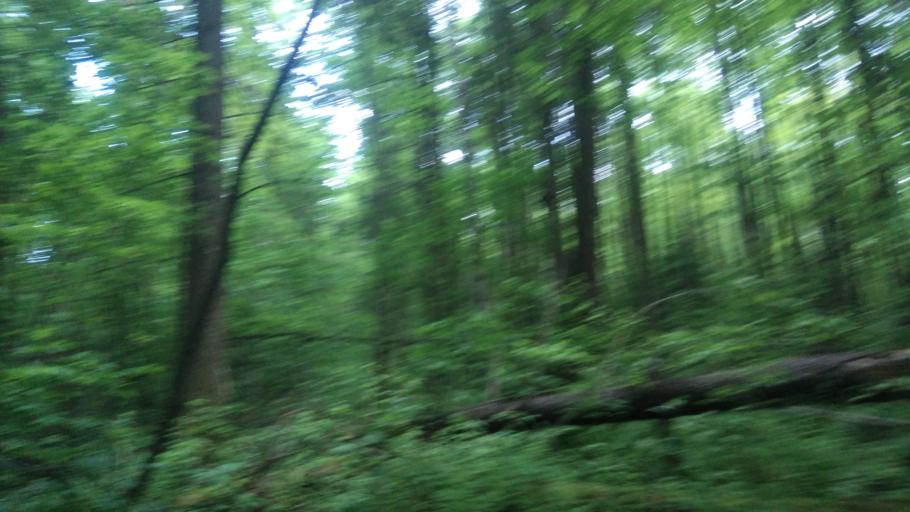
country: RU
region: Perm
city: Ferma
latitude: 57.9676
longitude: 56.3437
